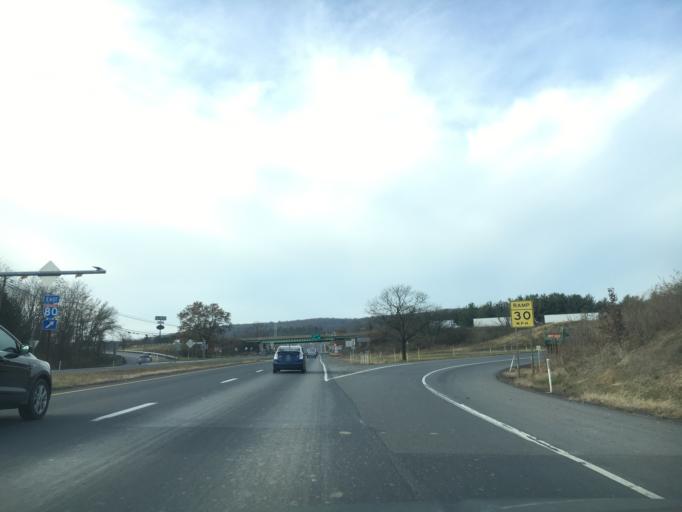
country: US
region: Pennsylvania
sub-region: Northumberland County
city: Riverside
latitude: 40.9953
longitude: -76.6420
